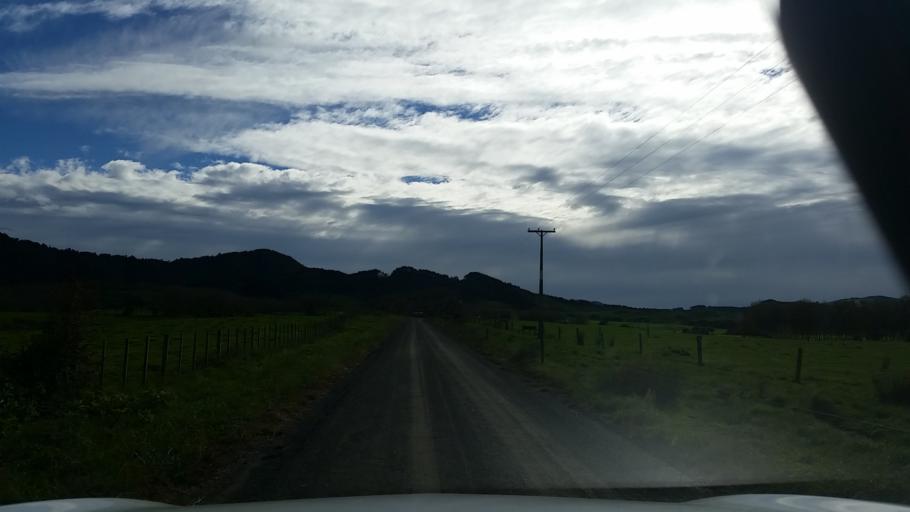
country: NZ
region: Waikato
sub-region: Hauraki District
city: Ngatea
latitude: -37.5106
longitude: 175.4082
